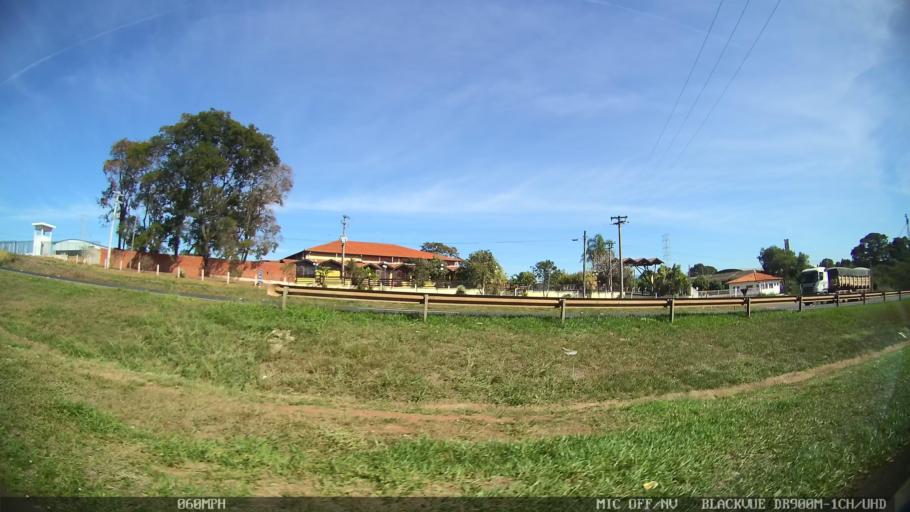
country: BR
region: Sao Paulo
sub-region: Pirassununga
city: Pirassununga
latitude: -22.0261
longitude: -47.4364
